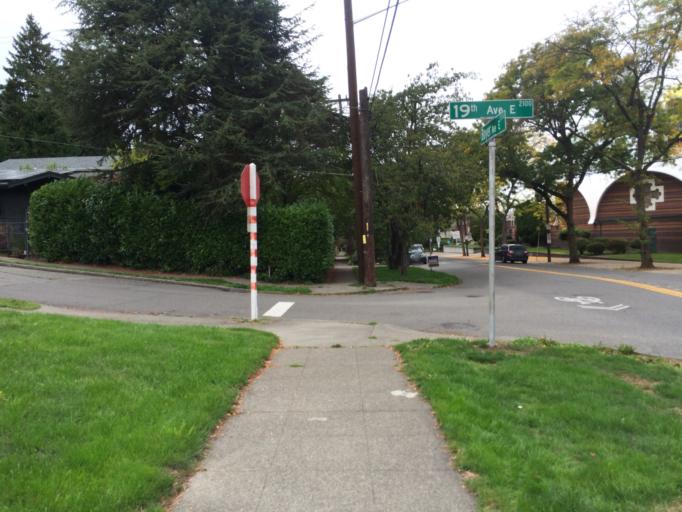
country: US
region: Washington
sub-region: King County
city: Seattle
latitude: 47.6379
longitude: -122.3072
